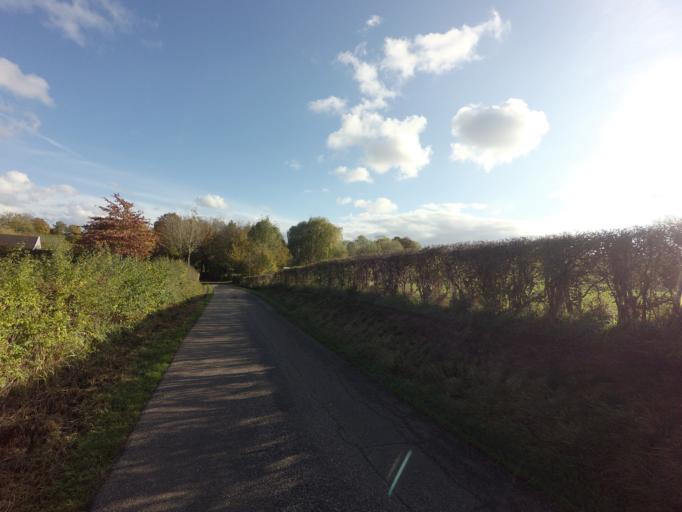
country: BE
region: Wallonia
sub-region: Province de Liege
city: Plombieres
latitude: 50.7618
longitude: 5.9106
